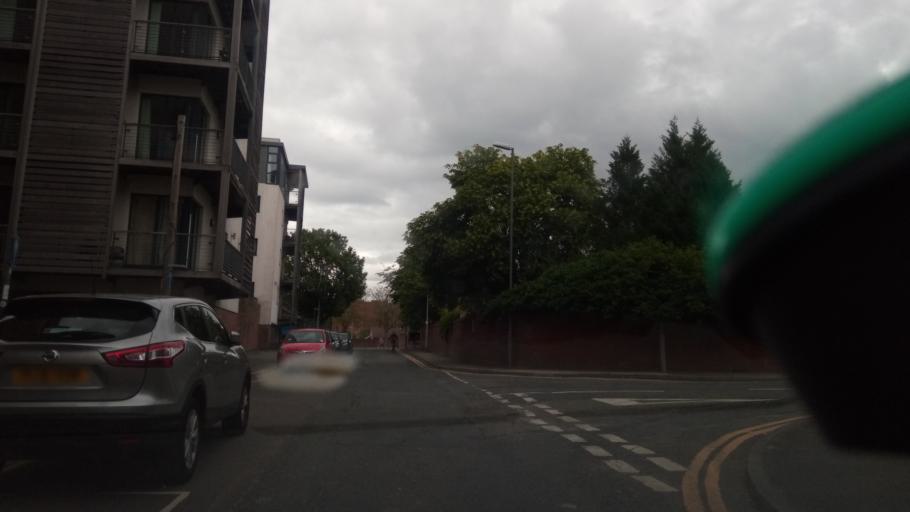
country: GB
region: England
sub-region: Liverpool
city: Liverpool
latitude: 53.3987
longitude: -2.9851
